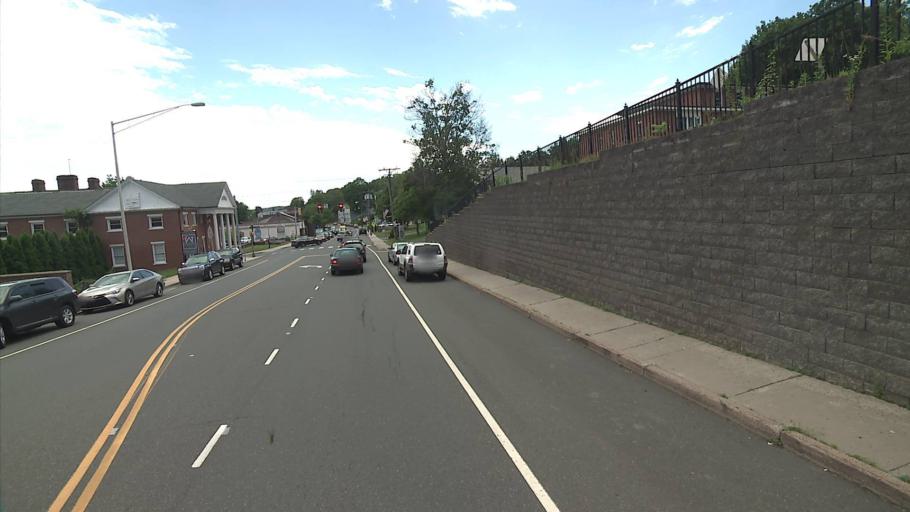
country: US
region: Connecticut
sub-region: Litchfield County
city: Watertown
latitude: 41.6034
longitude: -73.1168
